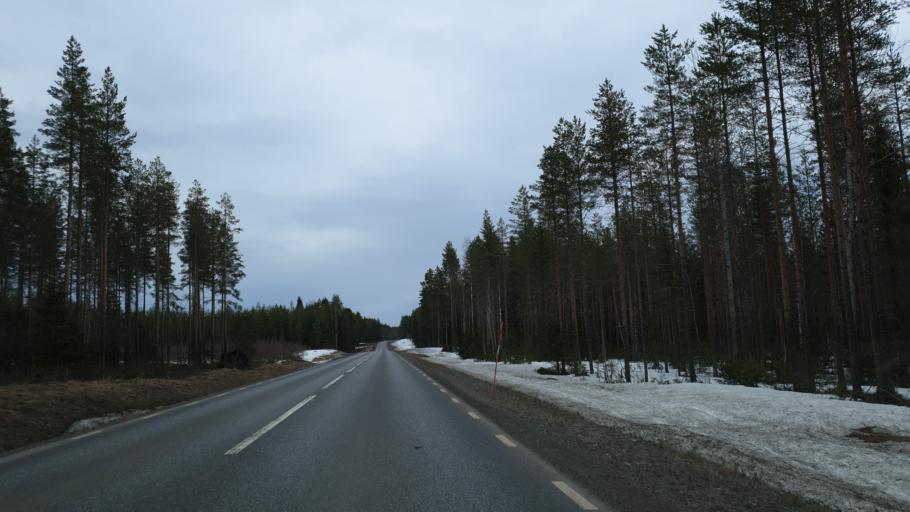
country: SE
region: Vaesterbotten
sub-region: Robertsfors Kommun
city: Robertsfors
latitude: 64.2117
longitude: 20.8837
